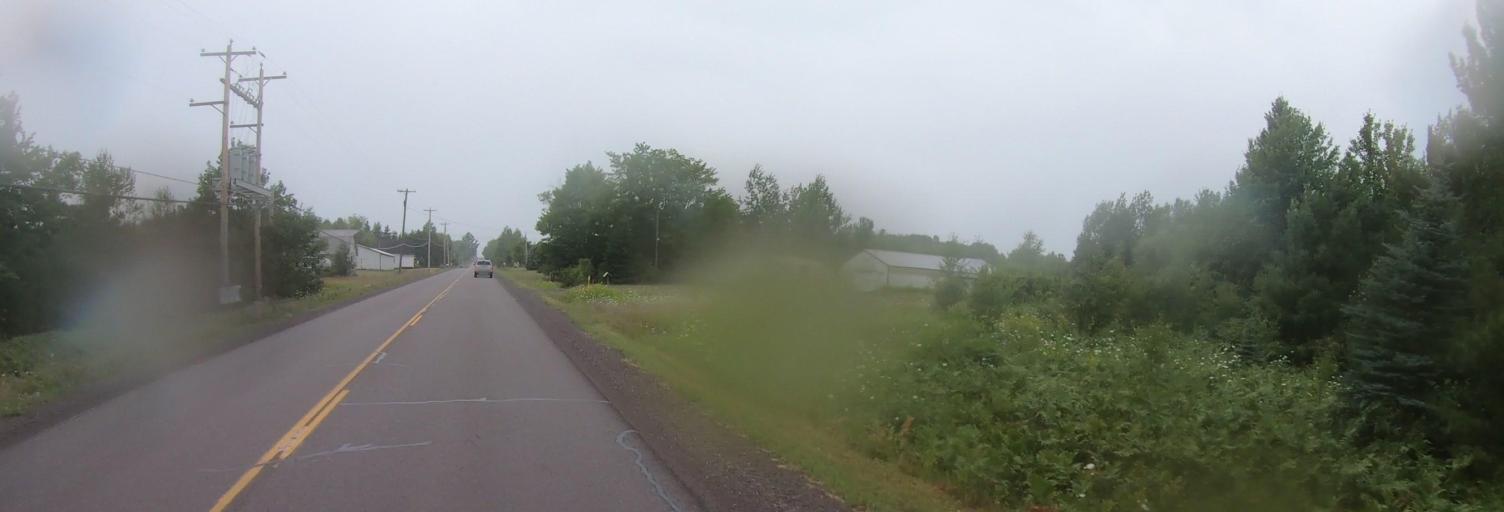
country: US
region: Michigan
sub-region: Houghton County
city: Dollar Bay
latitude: 47.0255
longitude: -88.5435
